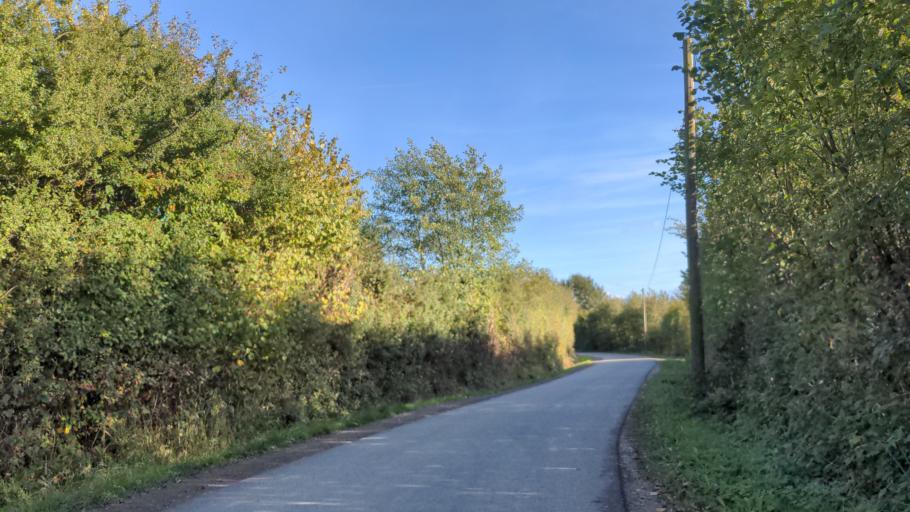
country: DE
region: Schleswig-Holstein
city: Manhagen
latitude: 54.1662
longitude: 10.9110
